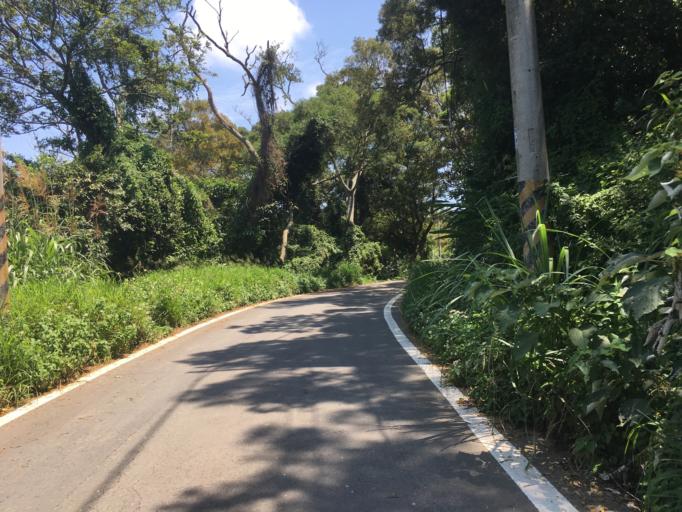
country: TW
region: Taiwan
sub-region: Hsinchu
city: Hsinchu
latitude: 24.7356
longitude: 120.9875
